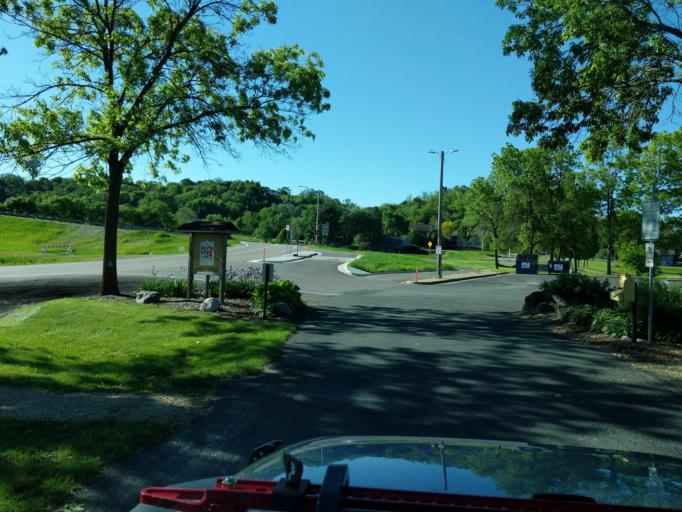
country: US
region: Wisconsin
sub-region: Pierce County
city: River Falls
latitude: 44.8648
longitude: -92.6092
